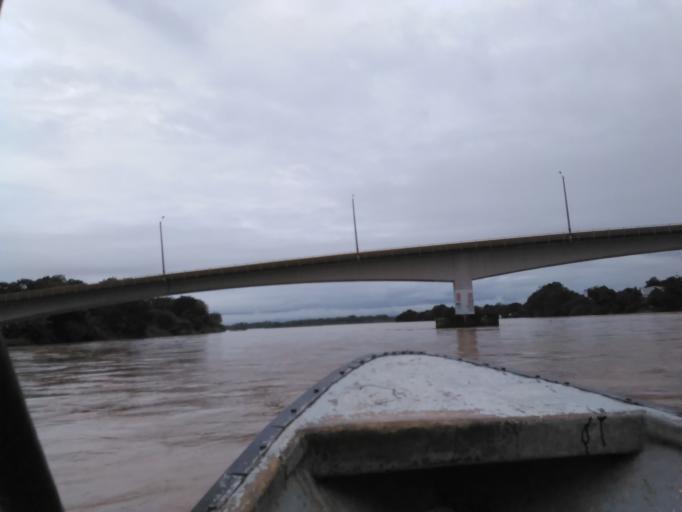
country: CO
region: Antioquia
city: El Bagre
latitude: 7.6066
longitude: -74.8111
